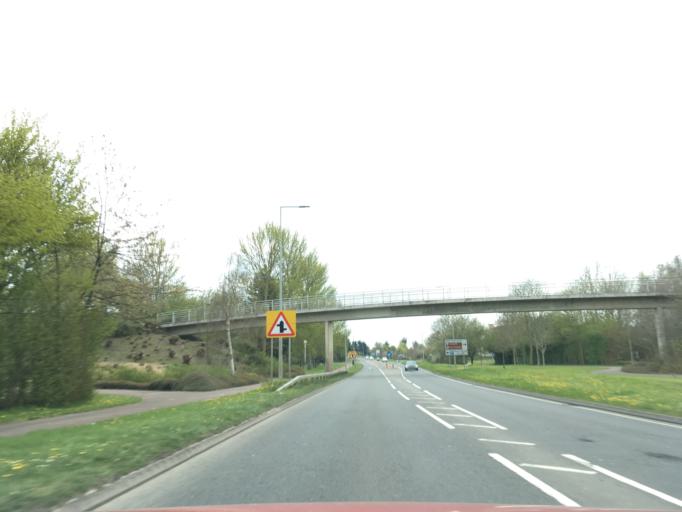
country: GB
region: England
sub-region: Milton Keynes
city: Newport Pagnell
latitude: 52.0585
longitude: -0.7291
